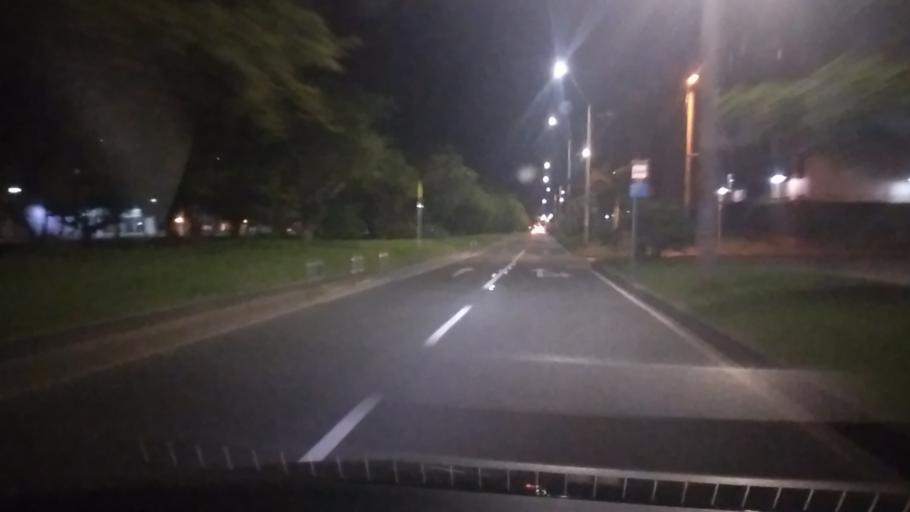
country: CO
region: Valle del Cauca
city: Cali
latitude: 3.3856
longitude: -76.5166
